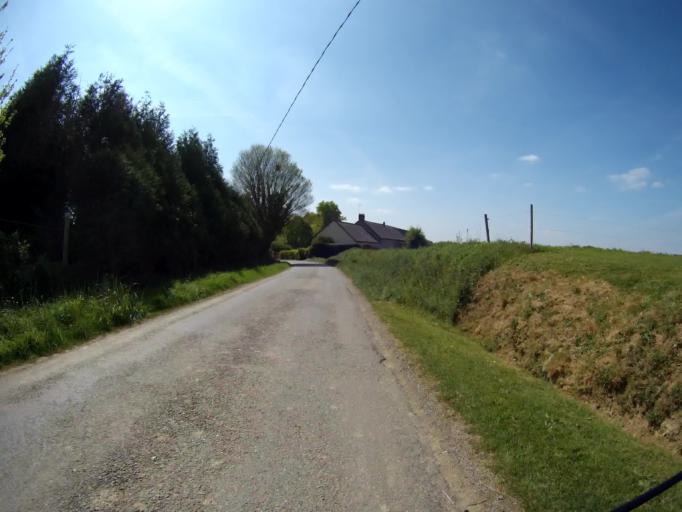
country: FR
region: Brittany
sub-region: Departement d'Ille-et-Vilaine
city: Vern-sur-Seiche
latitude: 48.0340
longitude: -1.6183
